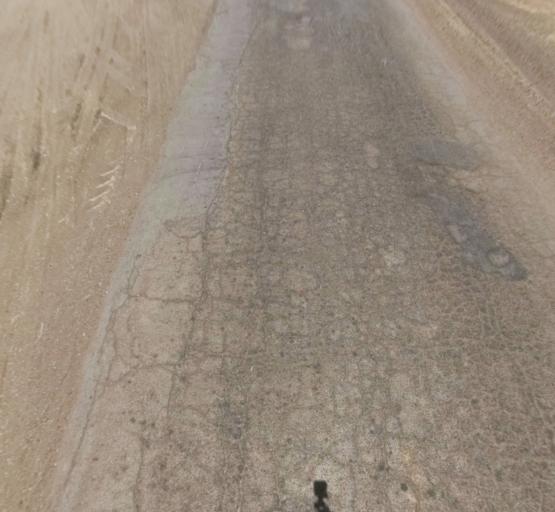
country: US
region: California
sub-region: Madera County
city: Chowchilla
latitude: 37.0937
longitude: -120.3289
